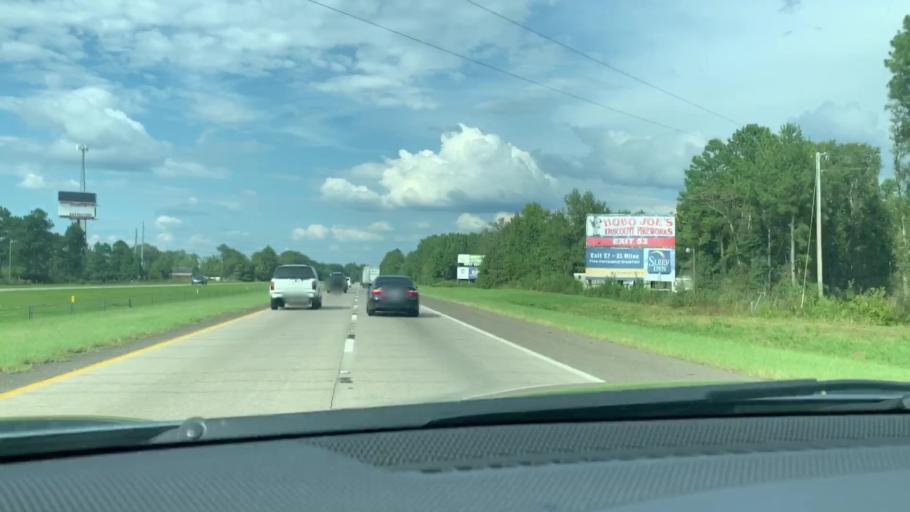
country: US
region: South Carolina
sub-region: Hampton County
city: Yemassee
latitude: 32.6809
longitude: -80.8818
